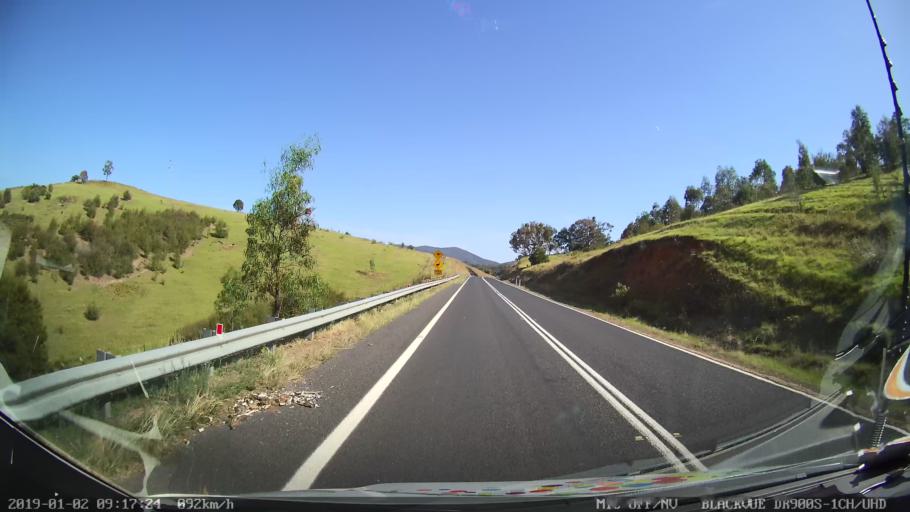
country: AU
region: New South Wales
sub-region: Tumut Shire
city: Tumut
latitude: -35.4409
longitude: 148.2868
